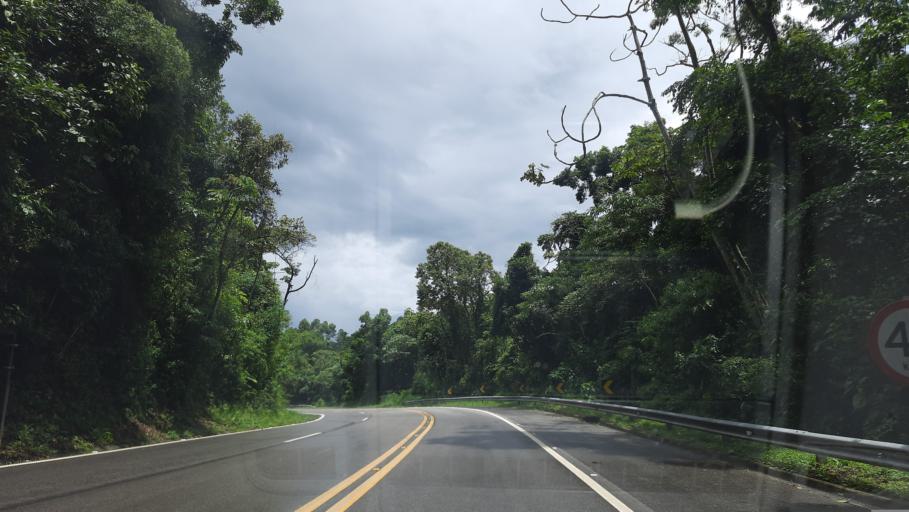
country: BR
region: Minas Gerais
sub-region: Pocos De Caldas
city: Pocos de Caldas
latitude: -21.8430
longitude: -46.6928
